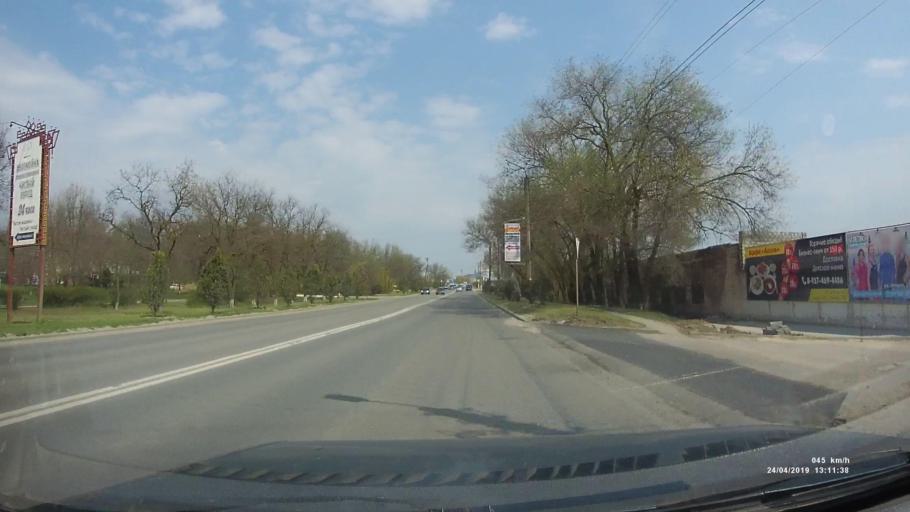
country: RU
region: Kalmykiya
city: Elista
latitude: 46.3126
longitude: 44.2962
